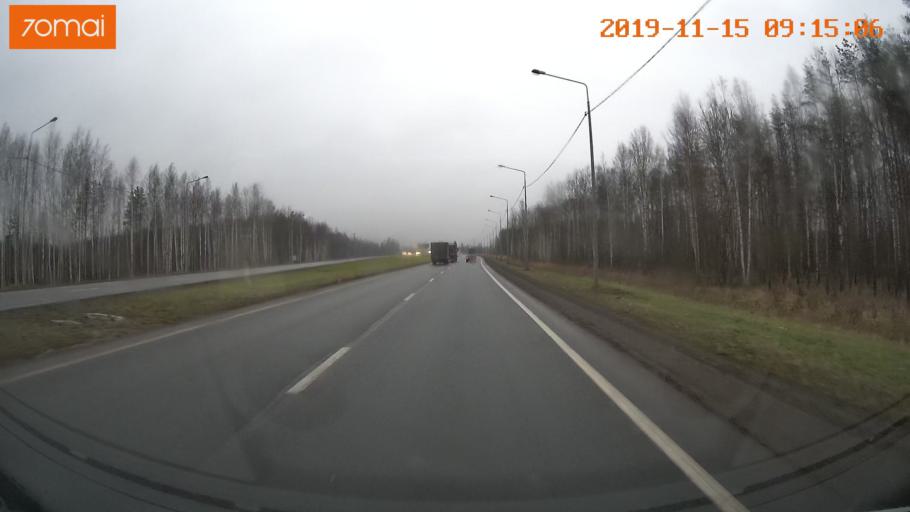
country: RU
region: Vologda
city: Tonshalovo
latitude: 59.2348
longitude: 37.9644
